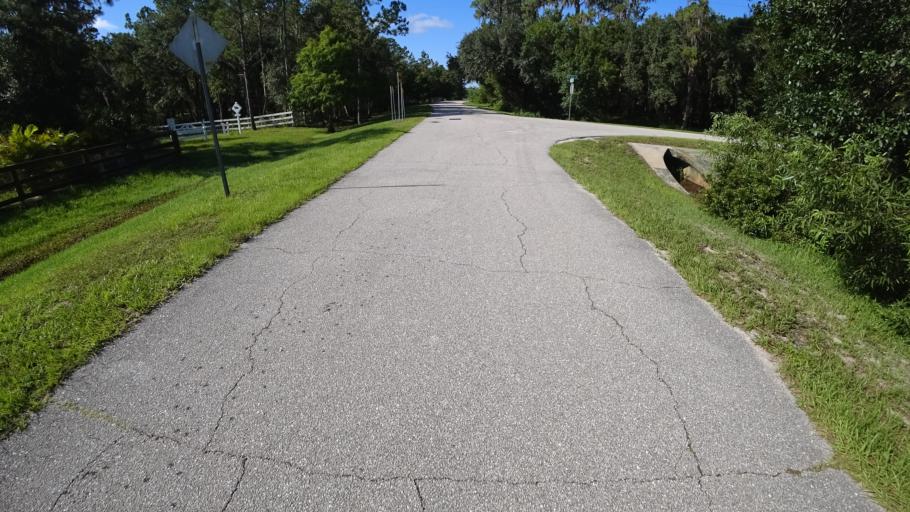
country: US
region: Florida
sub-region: Sarasota County
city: The Meadows
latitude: 27.4281
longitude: -82.3435
